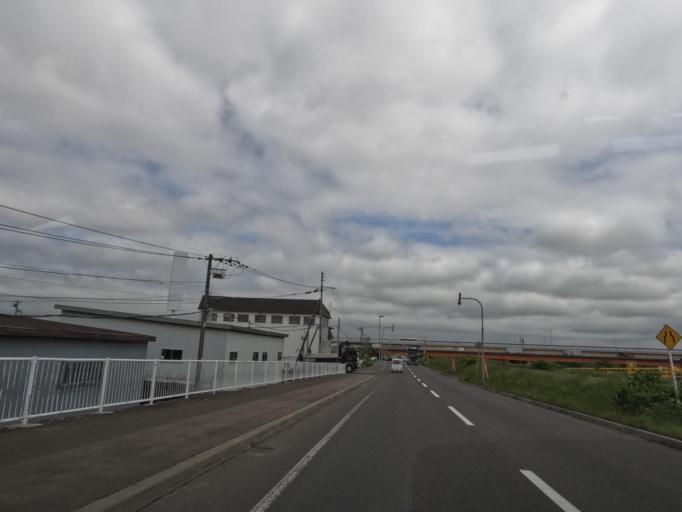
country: JP
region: Hokkaido
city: Sapporo
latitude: 43.0834
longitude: 141.4147
